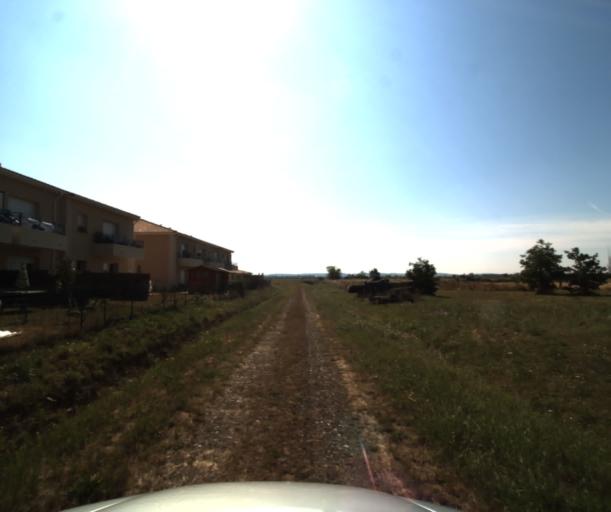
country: FR
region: Midi-Pyrenees
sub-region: Departement de la Haute-Garonne
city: Labastidette
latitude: 43.4579
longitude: 1.2497
